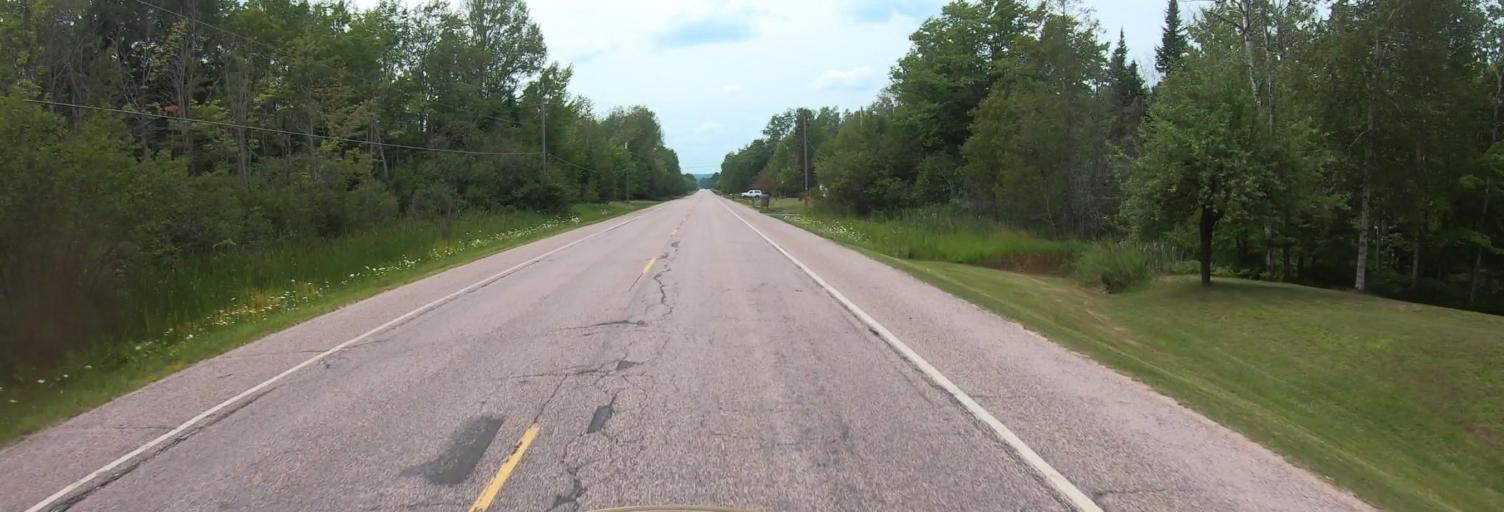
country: US
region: Michigan
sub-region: Marquette County
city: Harvey
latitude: 46.4637
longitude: -87.3299
